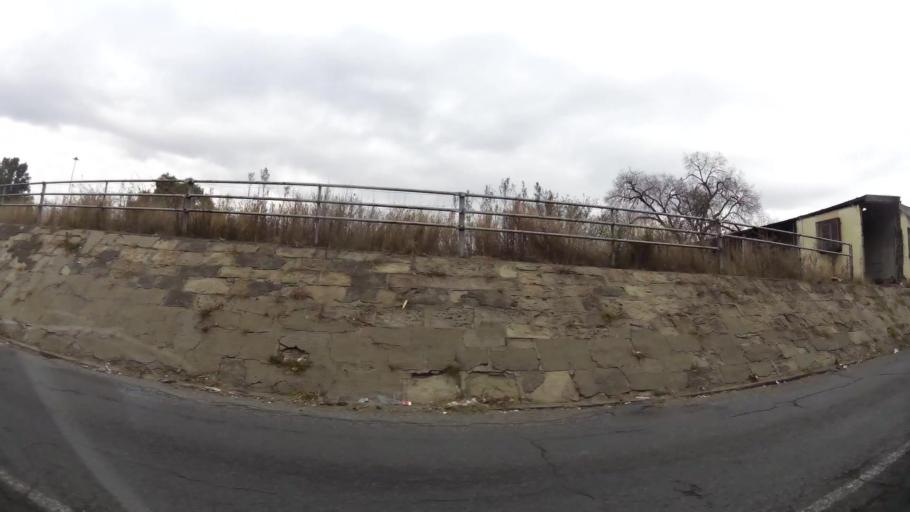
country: ZA
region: Orange Free State
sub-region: Fezile Dabi District Municipality
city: Kroonstad
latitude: -27.6595
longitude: 27.2313
